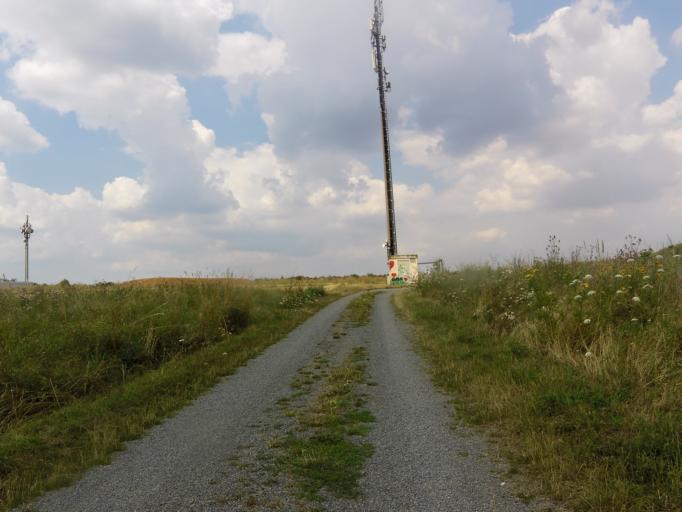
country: DE
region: Bavaria
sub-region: Regierungsbezirk Unterfranken
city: Eibelstadt
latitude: 49.7330
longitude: 9.9760
